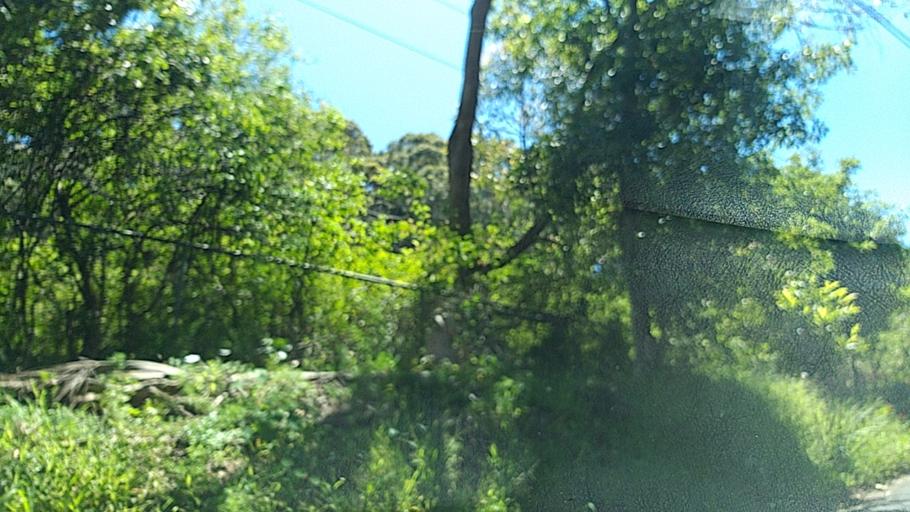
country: AU
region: New South Wales
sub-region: Wollongong
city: Bulli
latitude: -34.3044
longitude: 150.9322
